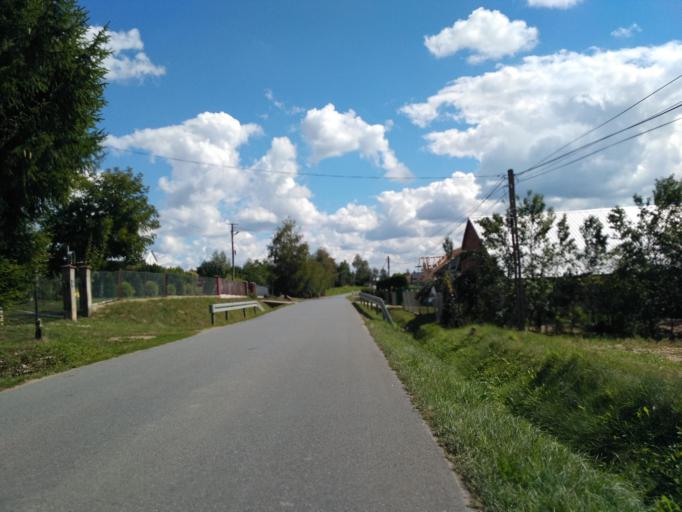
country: PL
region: Subcarpathian Voivodeship
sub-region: Powiat jasielski
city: Skolyszyn
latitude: 49.7817
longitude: 21.3553
